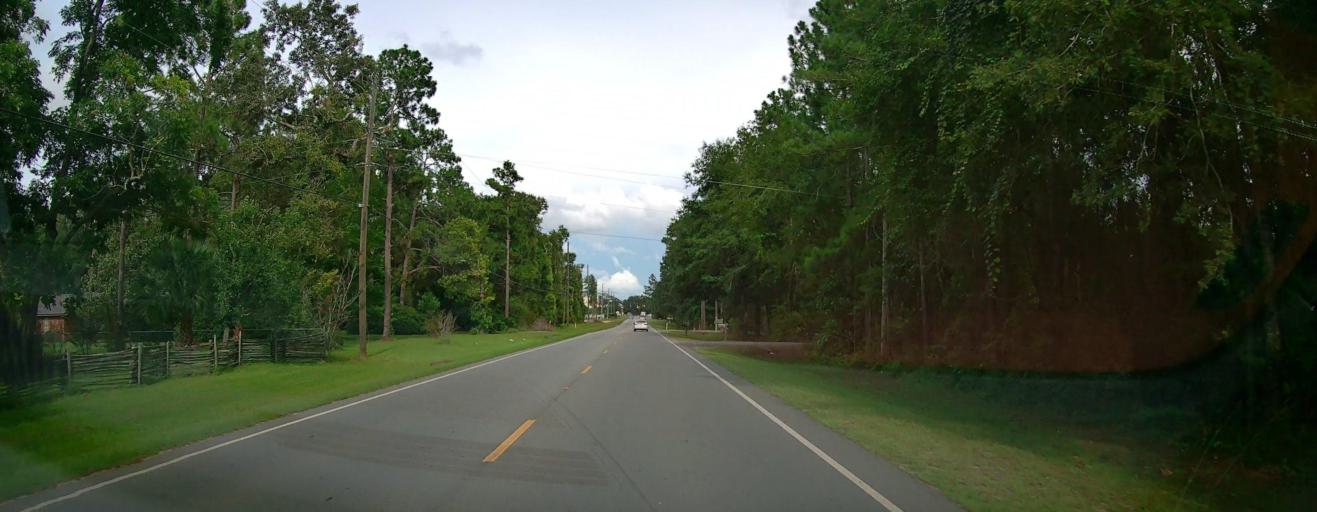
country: US
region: Georgia
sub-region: Wayne County
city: Jesup
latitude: 31.6622
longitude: -81.8535
